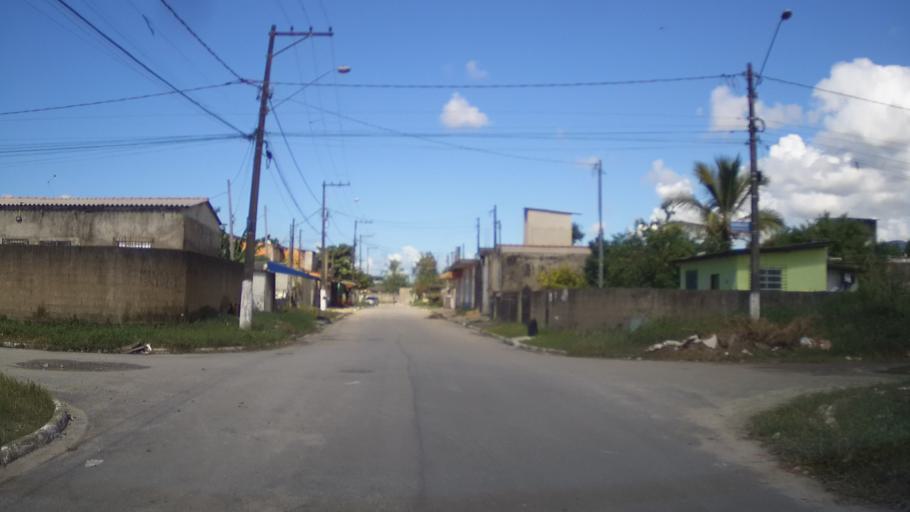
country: BR
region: Sao Paulo
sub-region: Praia Grande
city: Praia Grande
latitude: -24.0201
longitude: -46.5196
